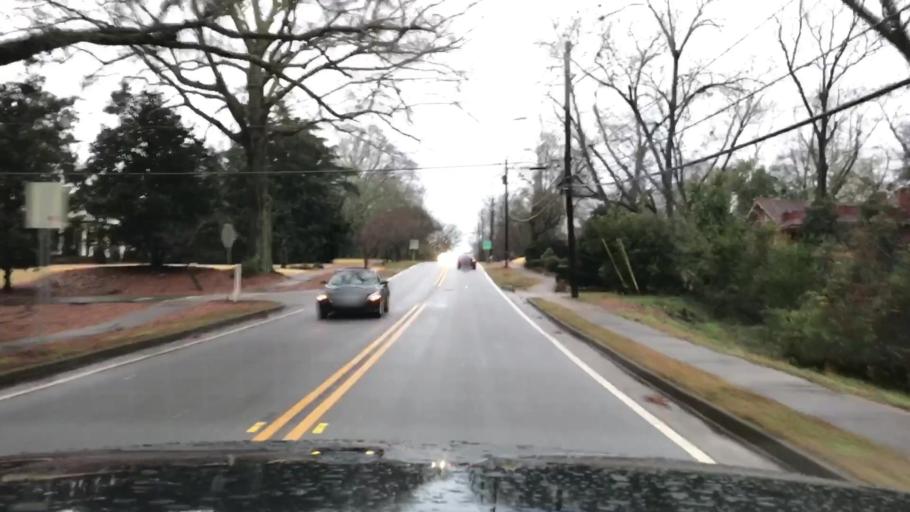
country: US
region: Georgia
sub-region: Morgan County
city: Madison
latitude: 33.5883
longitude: -83.4756
